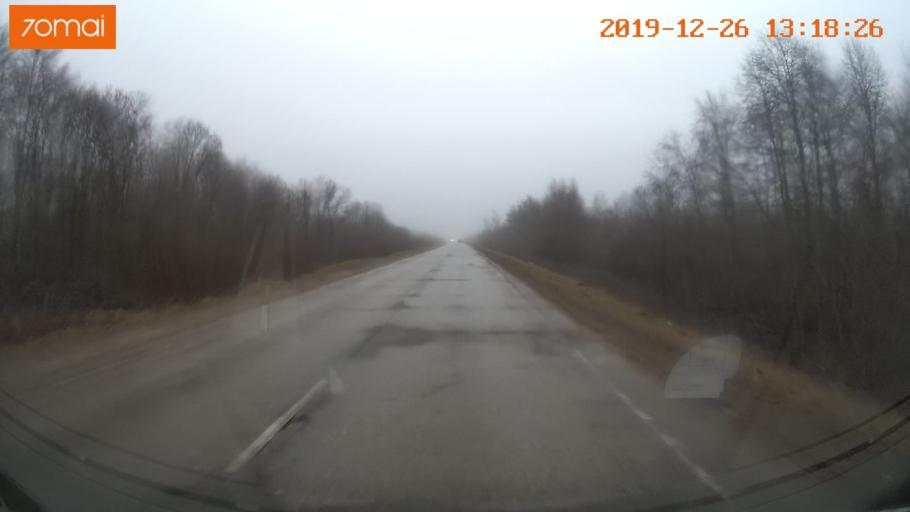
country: RU
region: Vologda
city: Cherepovets
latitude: 58.9550
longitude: 38.1224
